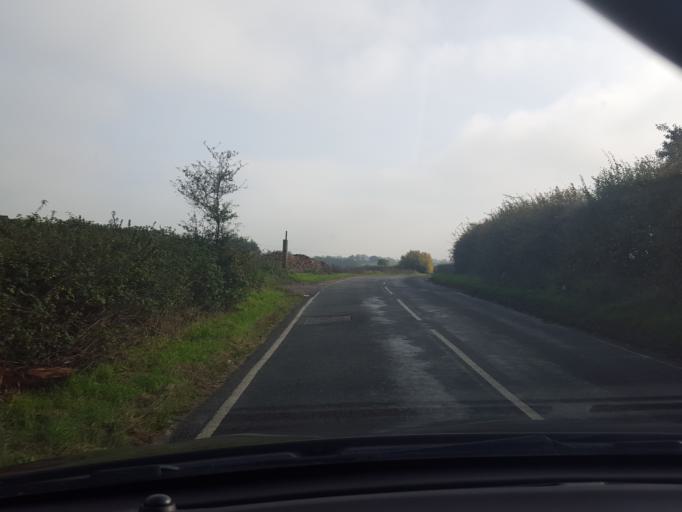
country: GB
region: England
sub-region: Essex
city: Mistley
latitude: 51.9336
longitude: 1.1277
